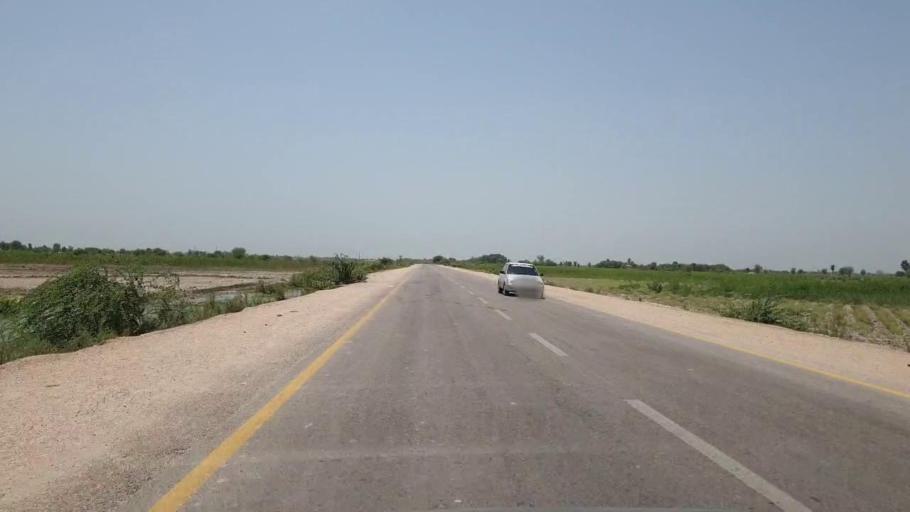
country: PK
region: Sindh
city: Sakrand
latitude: 26.1345
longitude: 68.3741
